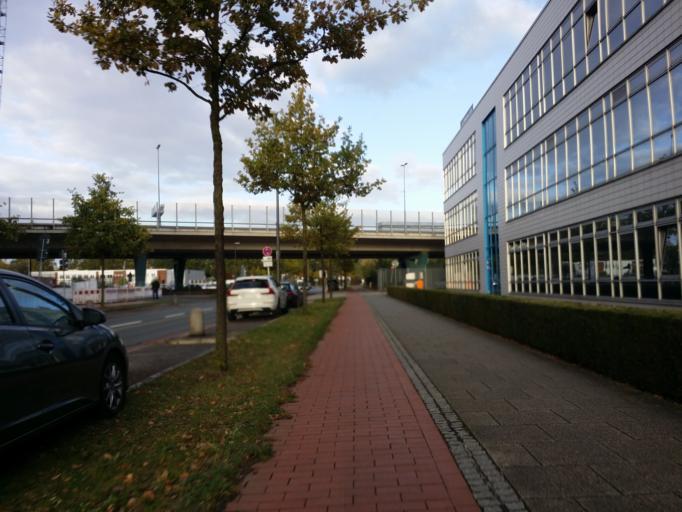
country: DE
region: Bremen
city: Bremen
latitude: 53.0550
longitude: 8.7936
